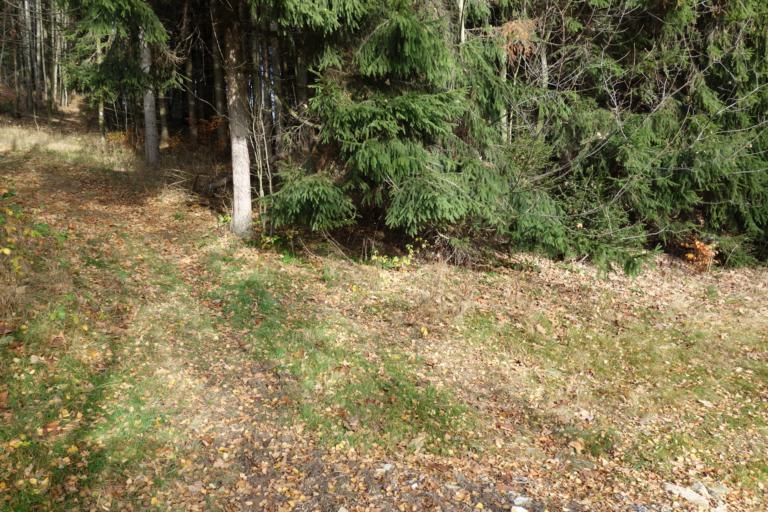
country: DE
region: Saxony
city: Barenstein
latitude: 50.5119
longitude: 13.0398
